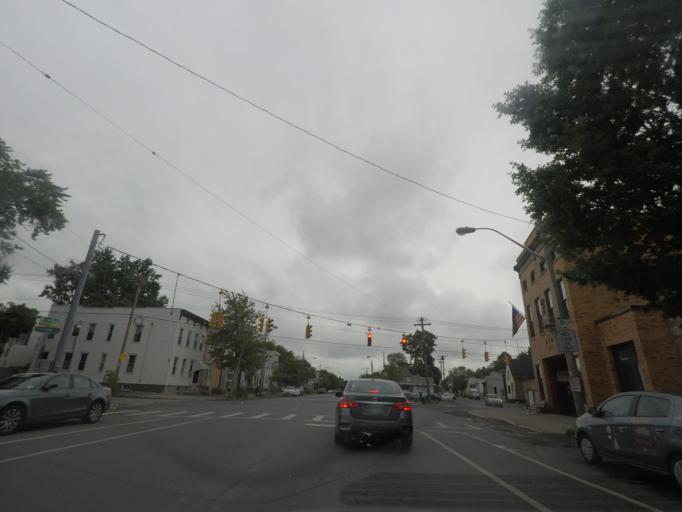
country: US
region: New York
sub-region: Albany County
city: West Albany
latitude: 42.6683
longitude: -73.7744
